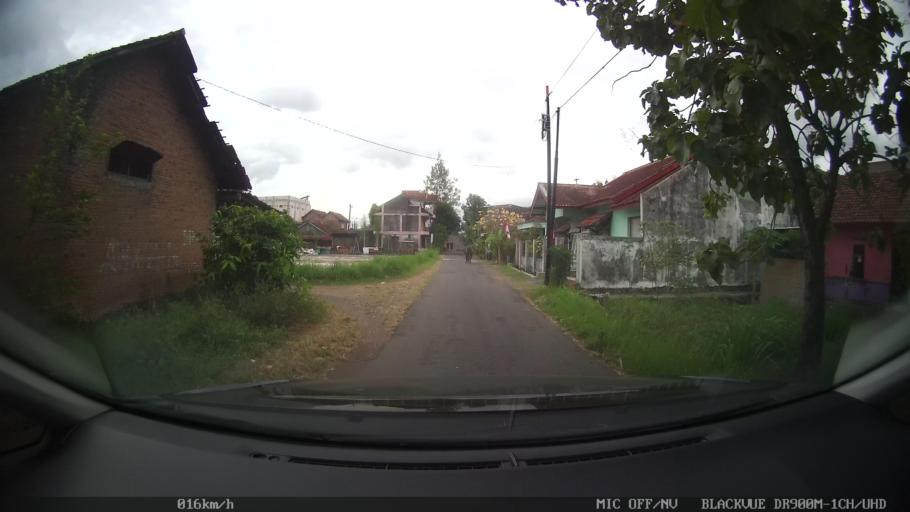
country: ID
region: Daerah Istimewa Yogyakarta
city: Sewon
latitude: -7.8336
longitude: 110.4115
